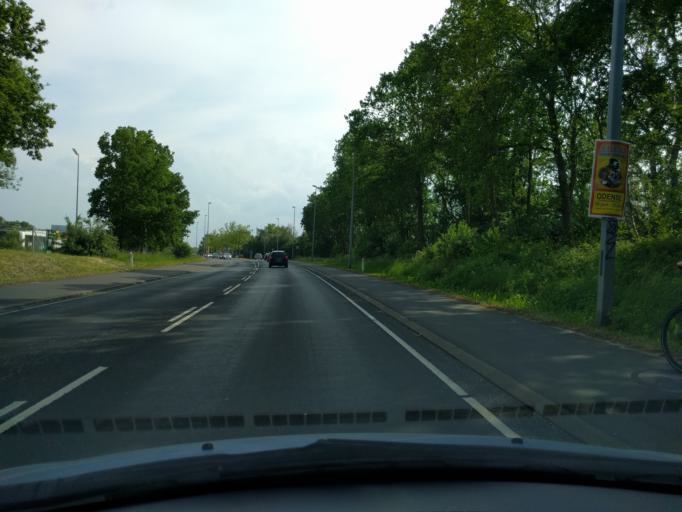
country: DK
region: South Denmark
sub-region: Odense Kommune
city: Odense
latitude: 55.4159
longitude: 10.3400
